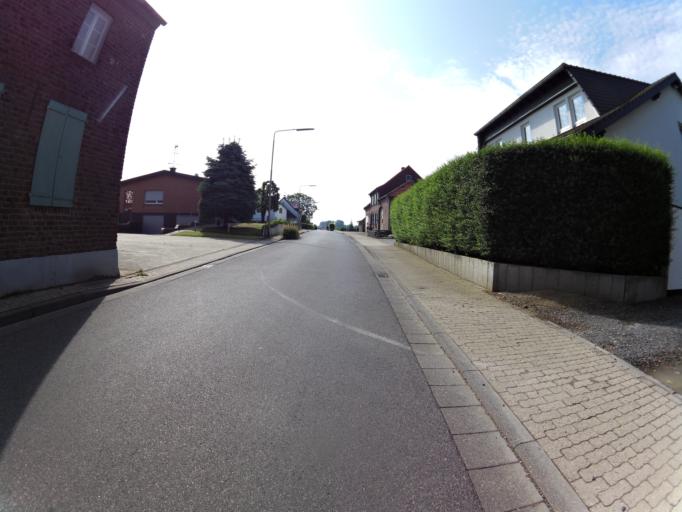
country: DE
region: North Rhine-Westphalia
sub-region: Regierungsbezirk Koln
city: Waldfeucht
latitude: 51.0731
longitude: 5.9981
